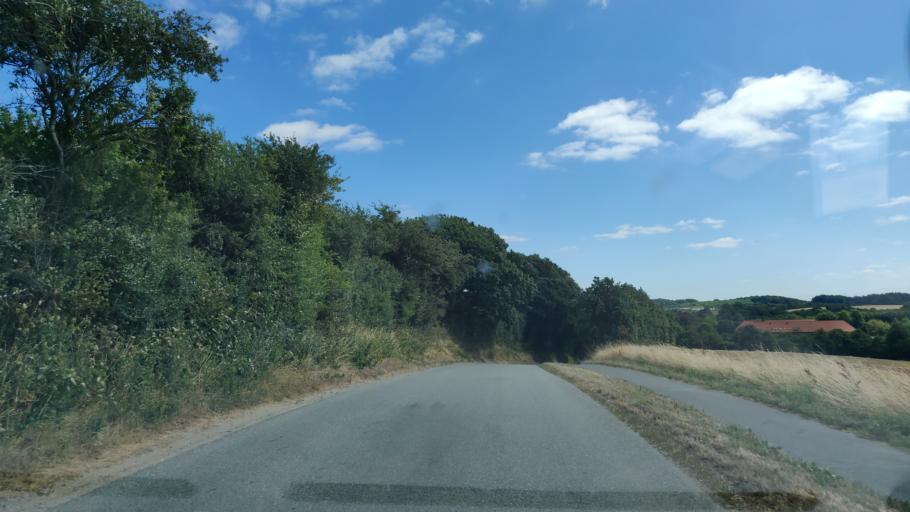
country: DK
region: South Denmark
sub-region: Kolding Kommune
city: Kolding
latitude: 55.5336
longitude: 9.5316
